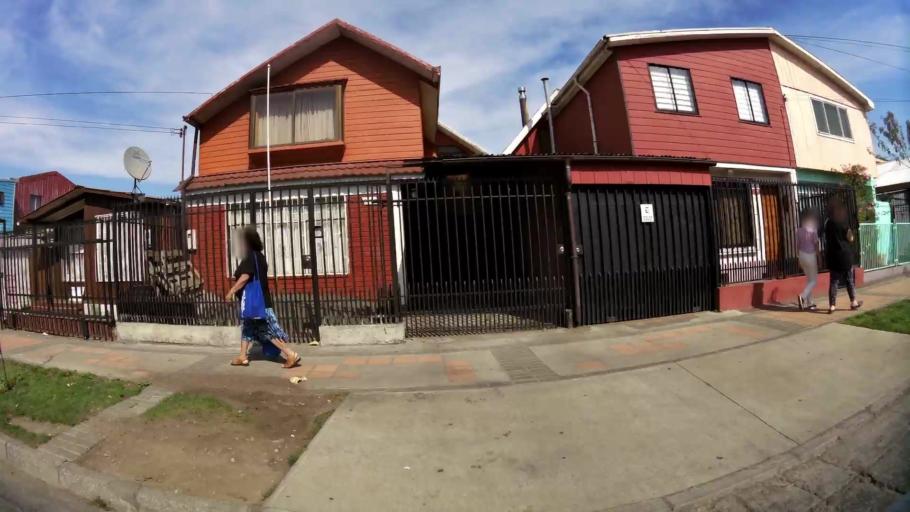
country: CL
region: Biobio
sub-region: Provincia de Concepcion
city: Talcahuano
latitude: -36.7864
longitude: -73.1041
